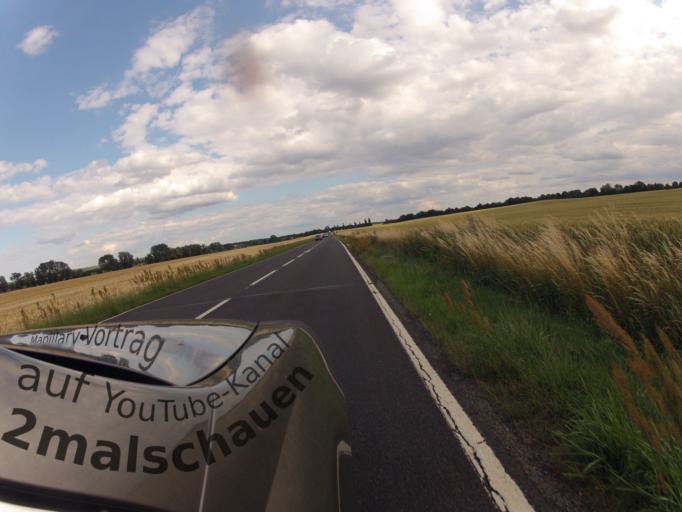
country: DE
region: Mecklenburg-Vorpommern
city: Seebad Bansin
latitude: 53.8935
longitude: 14.0712
